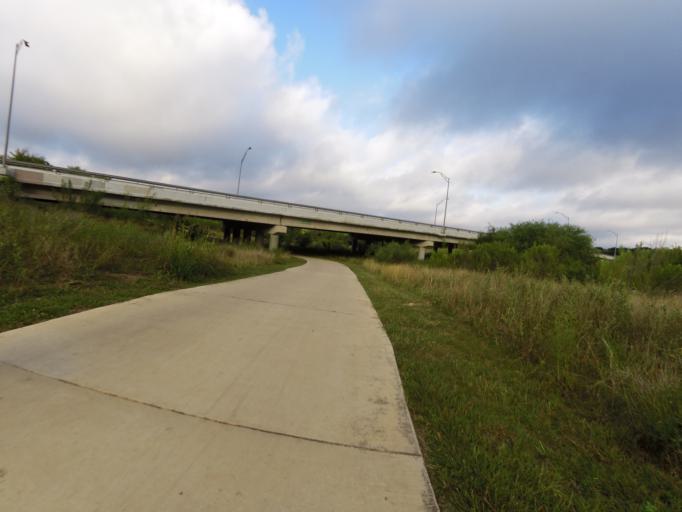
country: US
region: Texas
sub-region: Bexar County
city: Leon Valley
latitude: 29.5578
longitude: -98.6276
